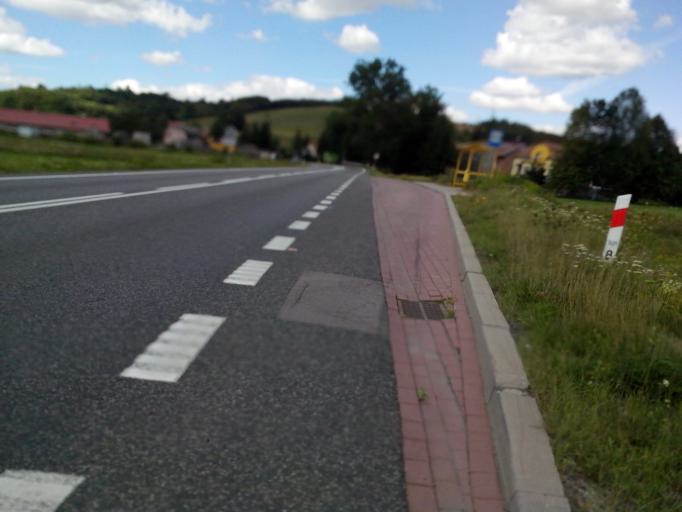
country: PL
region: Subcarpathian Voivodeship
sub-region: Powiat brzozowski
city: Domaradz
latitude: 49.8020
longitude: 21.9282
